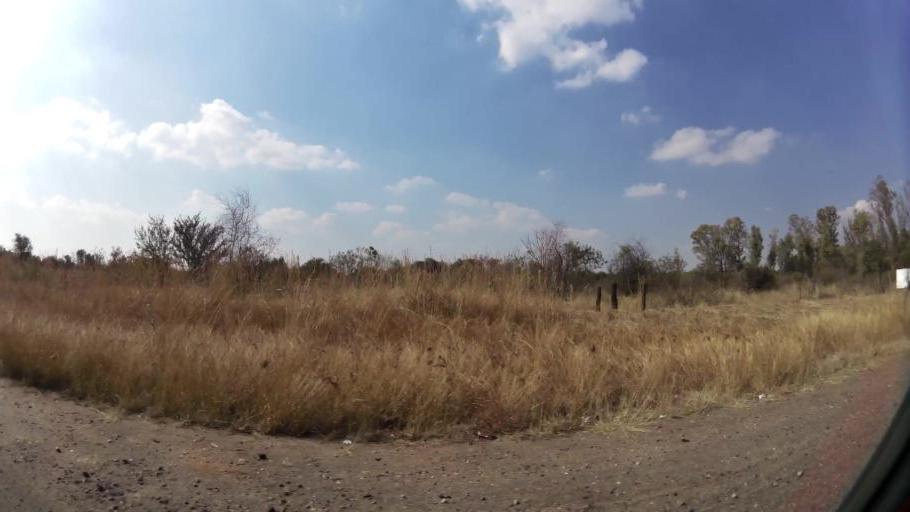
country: ZA
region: North-West
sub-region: Bojanala Platinum District Municipality
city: Rustenburg
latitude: -25.5172
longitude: 27.1016
